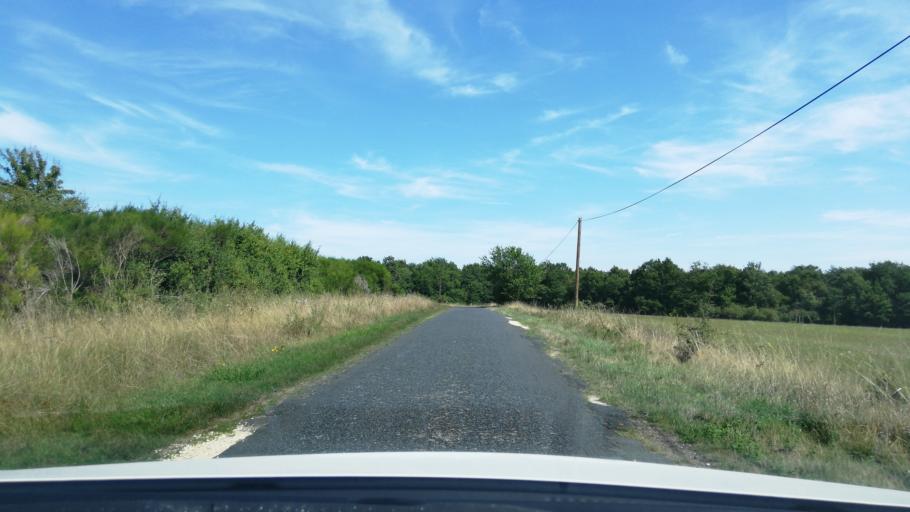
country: FR
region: Centre
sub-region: Departement d'Indre-et-Loire
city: Mazieres-de-Touraine
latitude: 47.3888
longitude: 0.4293
